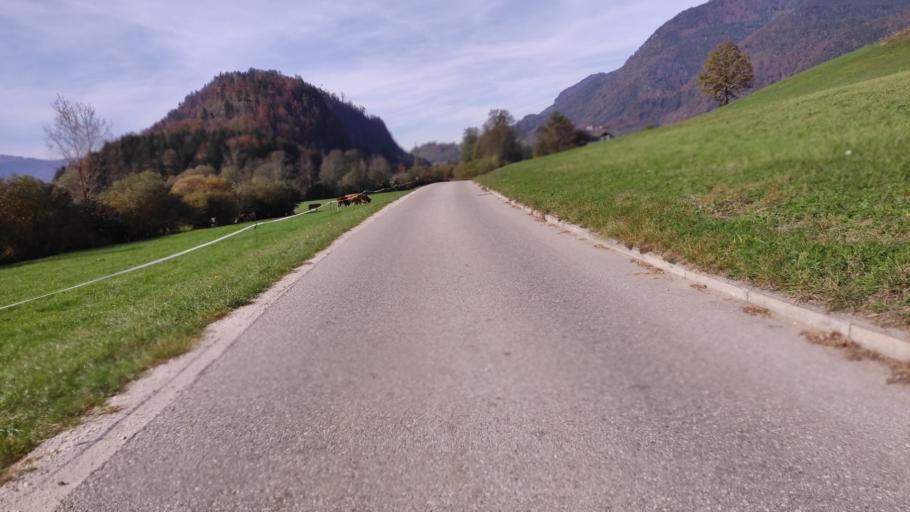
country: AT
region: Salzburg
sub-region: Politischer Bezirk Salzburg-Umgebung
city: Strobl
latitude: 47.7237
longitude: 13.5013
